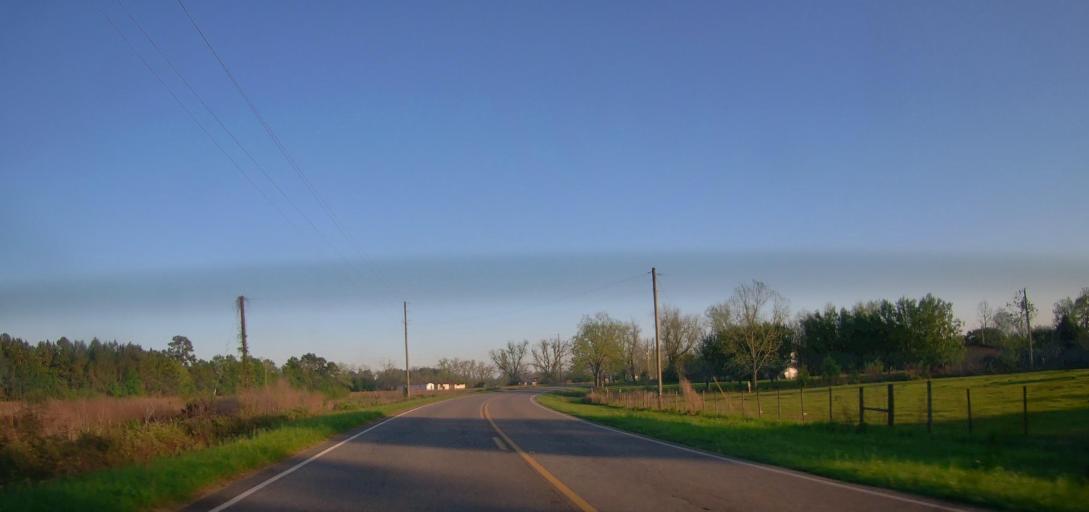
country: US
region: Georgia
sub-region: Irwin County
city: Ocilla
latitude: 31.6080
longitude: -83.2594
